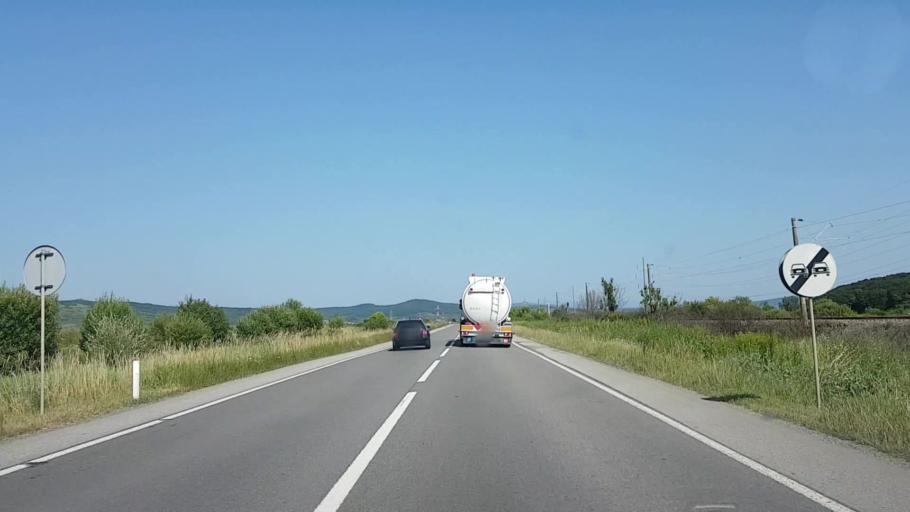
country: RO
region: Bistrita-Nasaud
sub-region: Comuna Sintereag
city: Cociu
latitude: 47.1824
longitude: 24.2410
